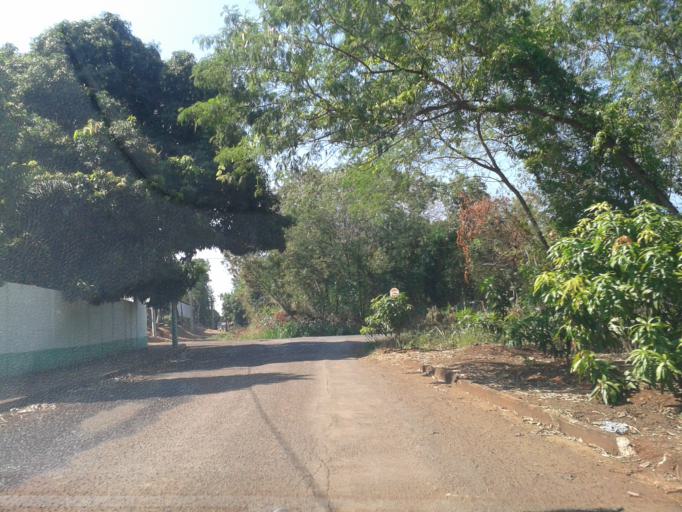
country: BR
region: Minas Gerais
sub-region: Ituiutaba
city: Ituiutaba
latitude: -18.9538
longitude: -49.4555
